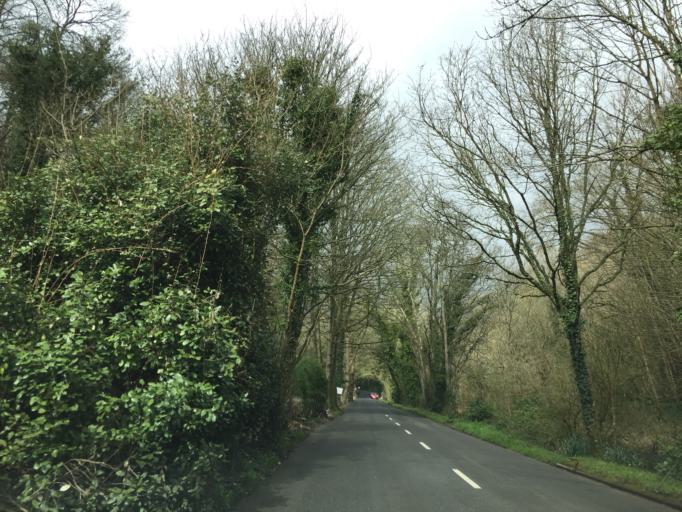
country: JE
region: St Helier
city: Saint Helier
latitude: 49.2162
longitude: -2.1722
